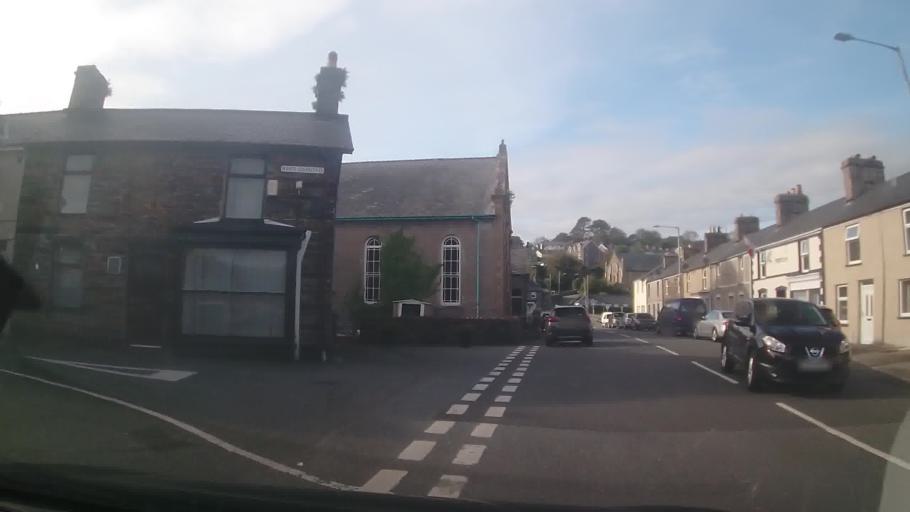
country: GB
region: Wales
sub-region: Gwynedd
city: Penrhyndeudraeth
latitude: 52.9306
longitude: -4.0677
